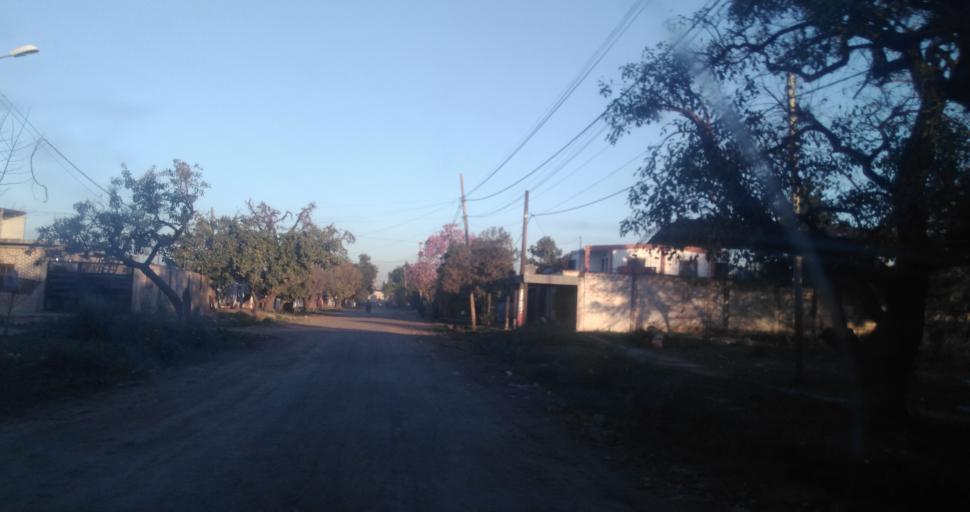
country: AR
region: Chaco
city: Fontana
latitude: -27.4285
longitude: -59.0082
